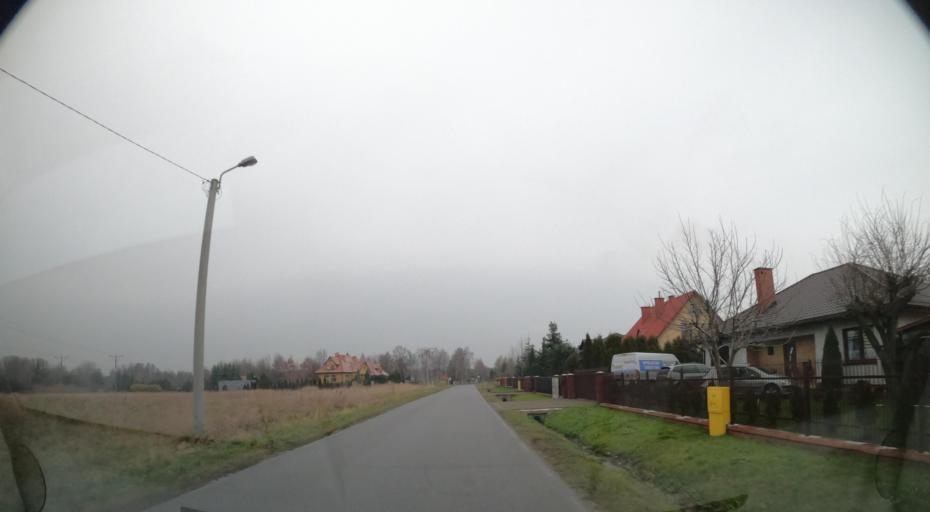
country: PL
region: Masovian Voivodeship
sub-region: Radom
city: Radom
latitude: 51.4181
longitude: 21.2239
